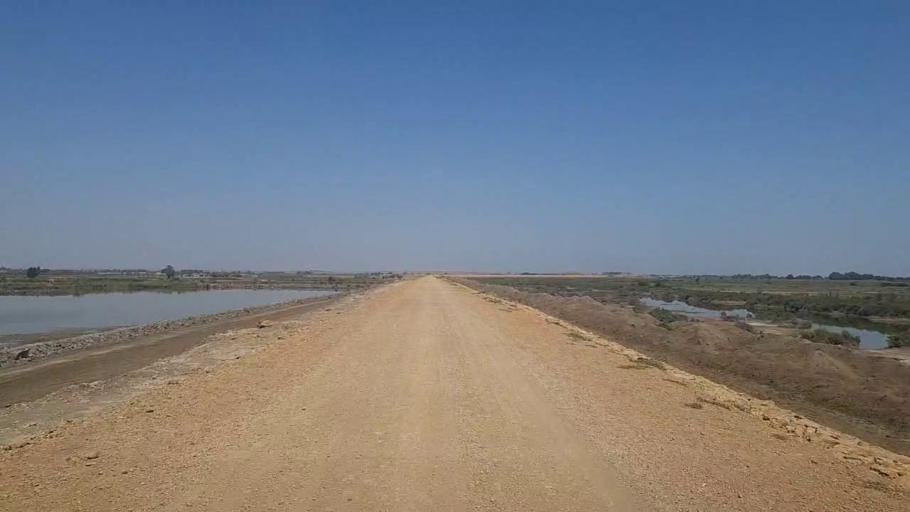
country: PK
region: Sindh
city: Thatta
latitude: 24.7921
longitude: 67.9978
